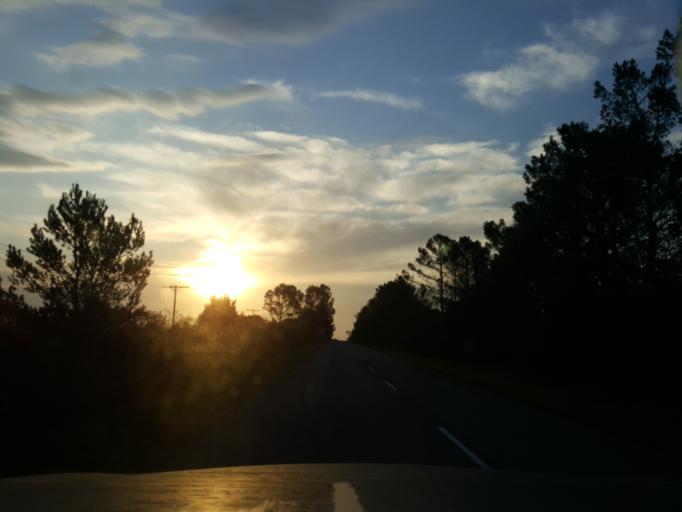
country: ZA
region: Eastern Cape
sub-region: Cacadu District Municipality
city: Grahamstown
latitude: -33.4552
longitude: 26.4947
